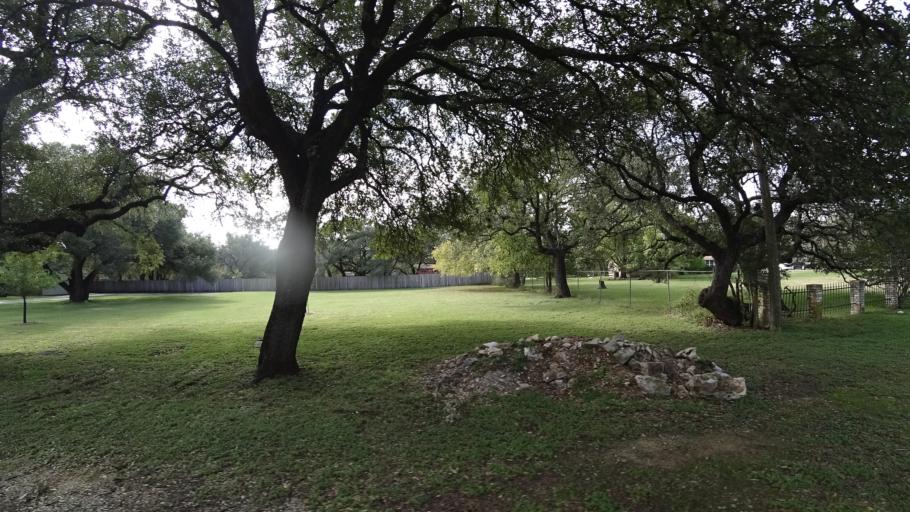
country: US
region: Texas
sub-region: Travis County
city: Wells Branch
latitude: 30.4313
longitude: -97.7085
